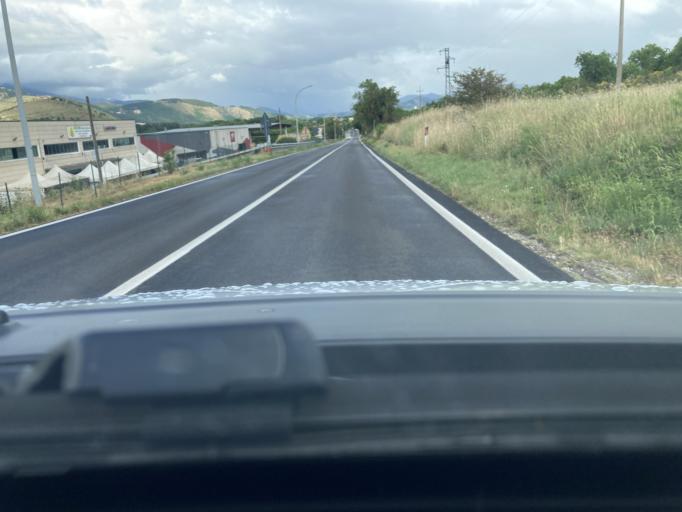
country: IT
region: Abruzzo
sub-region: Provincia dell' Aquila
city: San Demetrio Ne' Vestini
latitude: 42.2934
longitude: 13.5408
